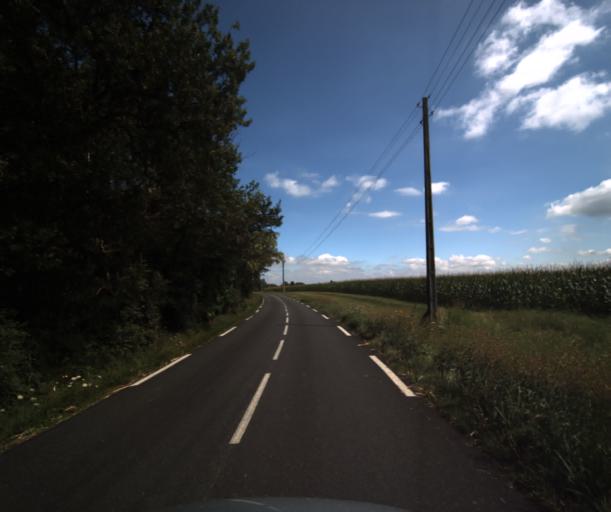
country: FR
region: Midi-Pyrenees
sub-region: Departement de la Haute-Garonne
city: Lacasse
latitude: 43.3860
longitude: 1.2489
